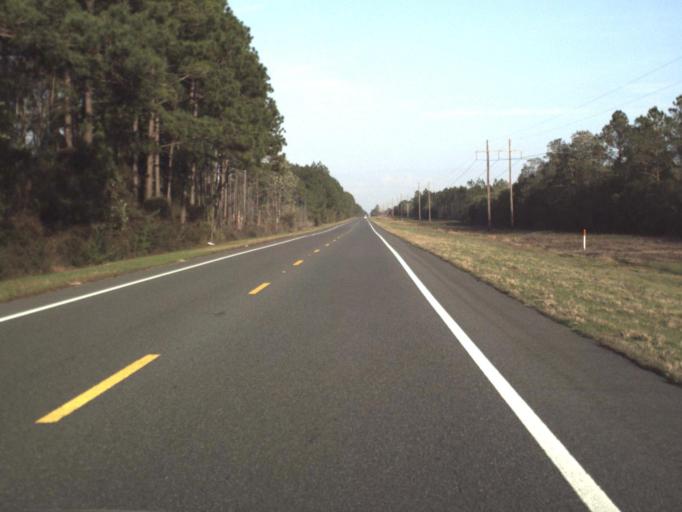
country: US
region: Florida
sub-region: Bay County
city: Laguna Beach
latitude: 30.4399
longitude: -85.8020
